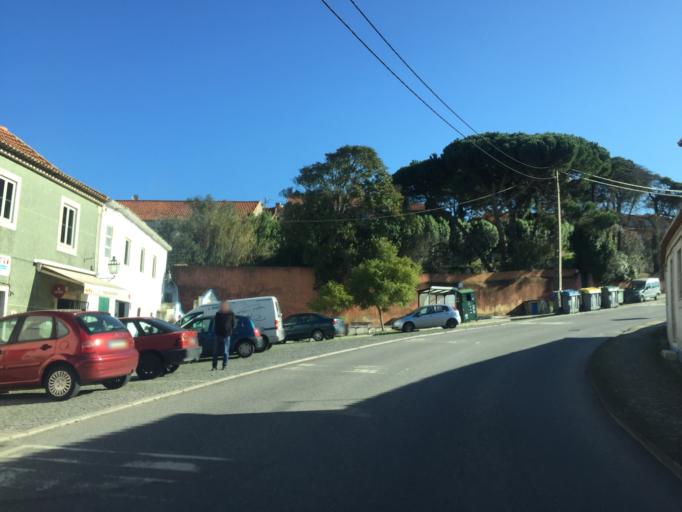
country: PT
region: Lisbon
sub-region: Sintra
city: Almargem
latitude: 38.8251
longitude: -9.2954
